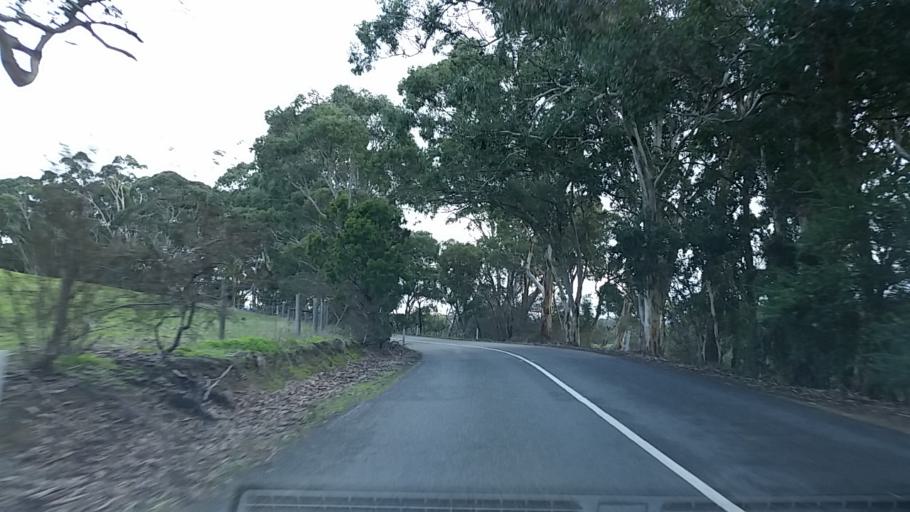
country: AU
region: South Australia
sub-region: Mount Barker
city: Little Hampton
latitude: -35.0765
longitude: 138.8190
